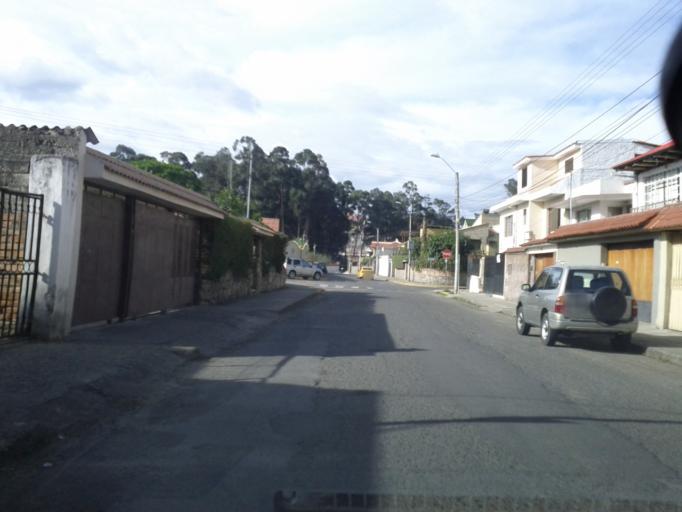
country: EC
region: Azuay
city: Cuenca
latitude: -2.8973
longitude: -79.0173
